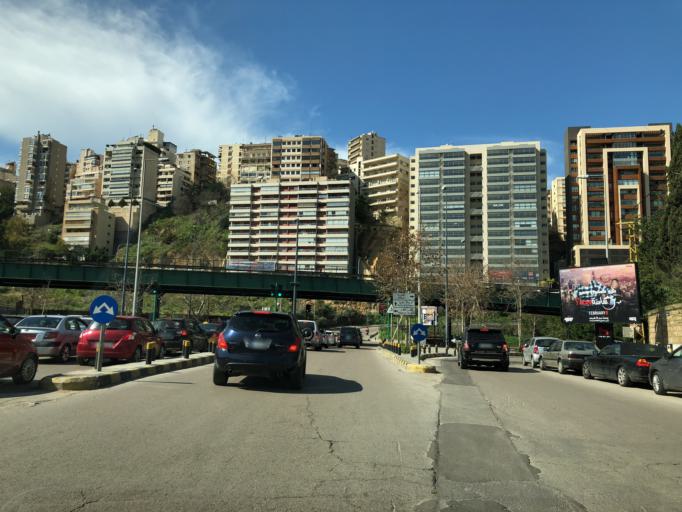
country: LB
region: Mont-Liban
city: Jdaidet el Matn
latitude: 33.8841
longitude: 35.5310
